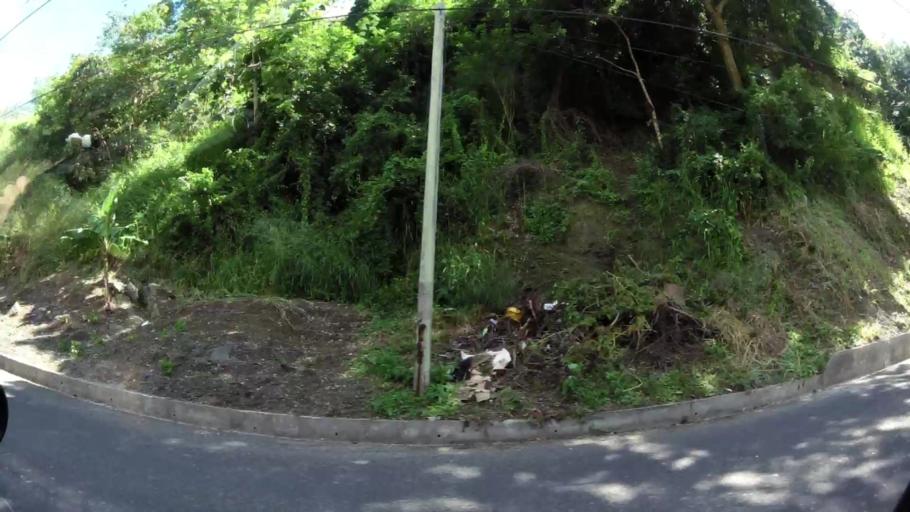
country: TT
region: Tobago
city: Scarborough
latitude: 11.2328
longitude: -60.7388
